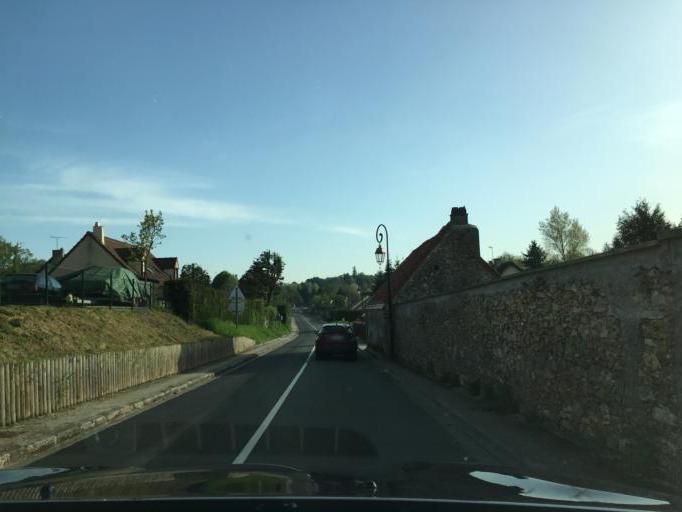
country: FR
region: Centre
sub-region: Departement d'Eure-et-Loir
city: Epernon
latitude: 48.6479
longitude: 1.6869
